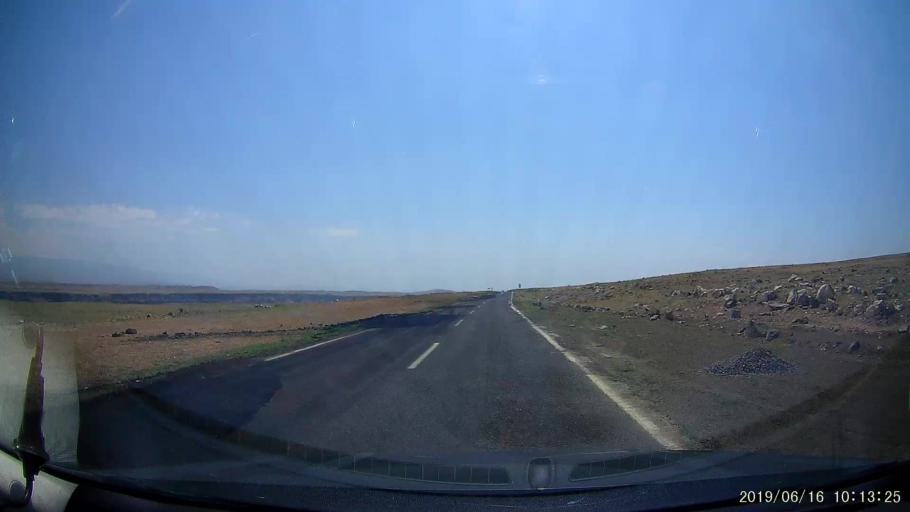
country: TR
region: Igdir
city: Tuzluca
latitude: 40.1927
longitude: 43.6423
